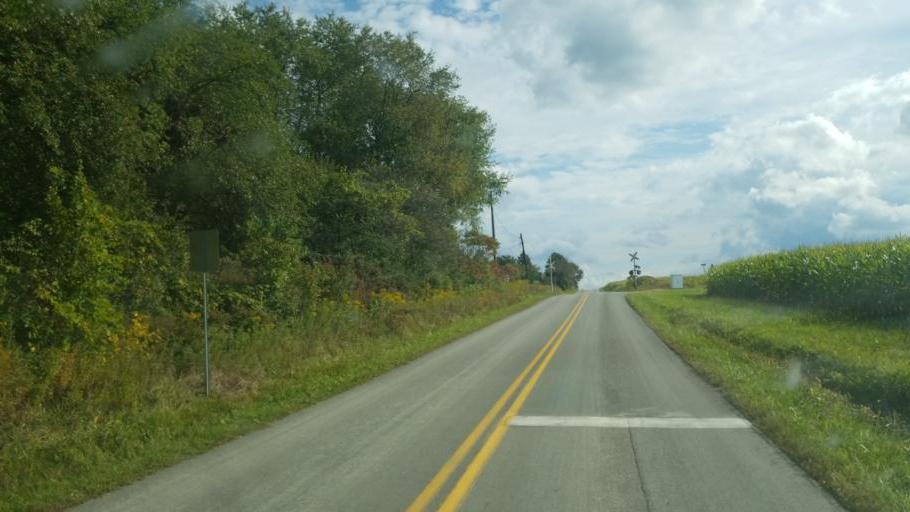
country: US
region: Pennsylvania
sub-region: Crawford County
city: Conneaut Lakeshore
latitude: 41.5158
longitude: -80.3375
